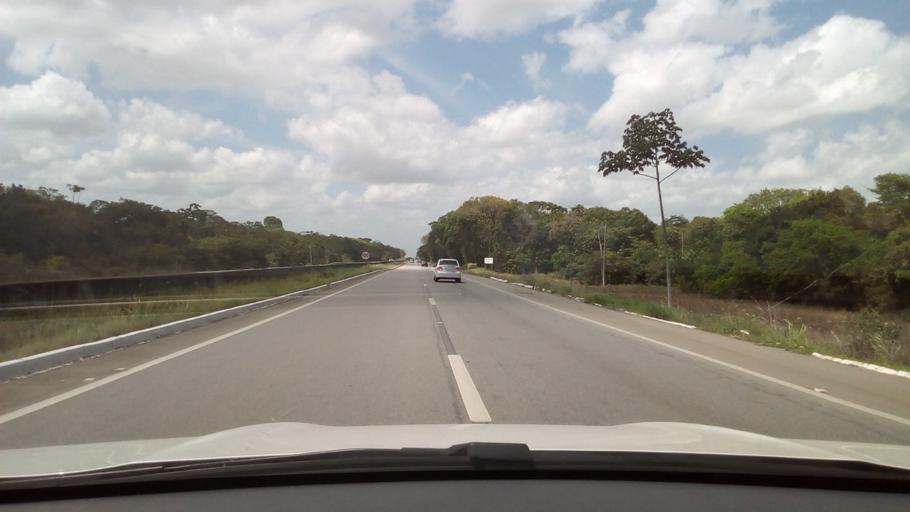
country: BR
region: Paraiba
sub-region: Mamanguape
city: Mamanguape
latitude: -6.9848
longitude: -35.0738
